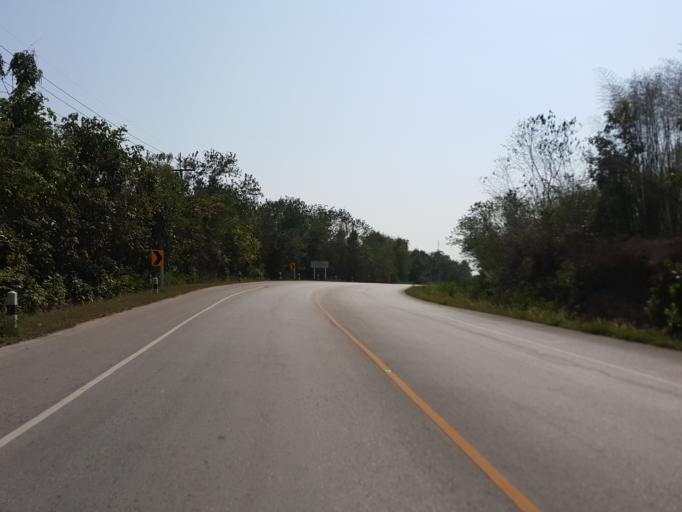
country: TH
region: Lampang
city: Chae Hom
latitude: 18.7652
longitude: 99.5737
